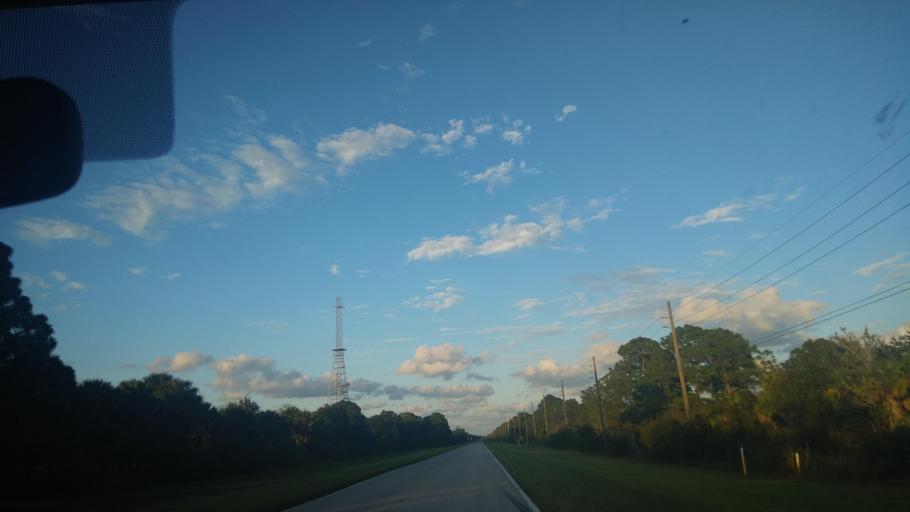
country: US
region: Florida
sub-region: Indian River County
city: Fellsmere
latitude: 27.7479
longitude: -80.6303
